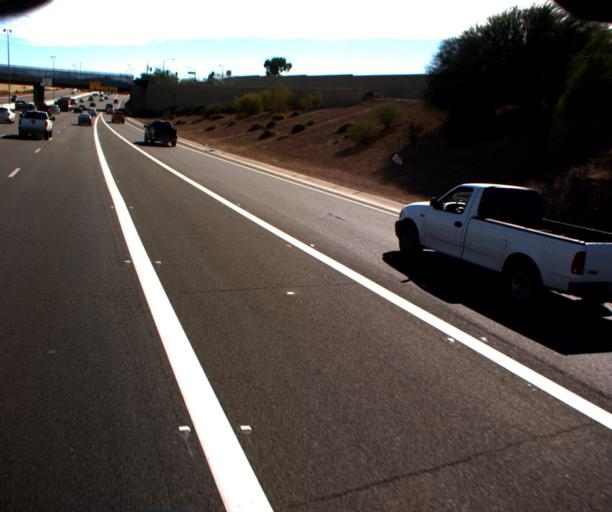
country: US
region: Arizona
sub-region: Maricopa County
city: Glendale
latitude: 33.6695
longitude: -112.0936
